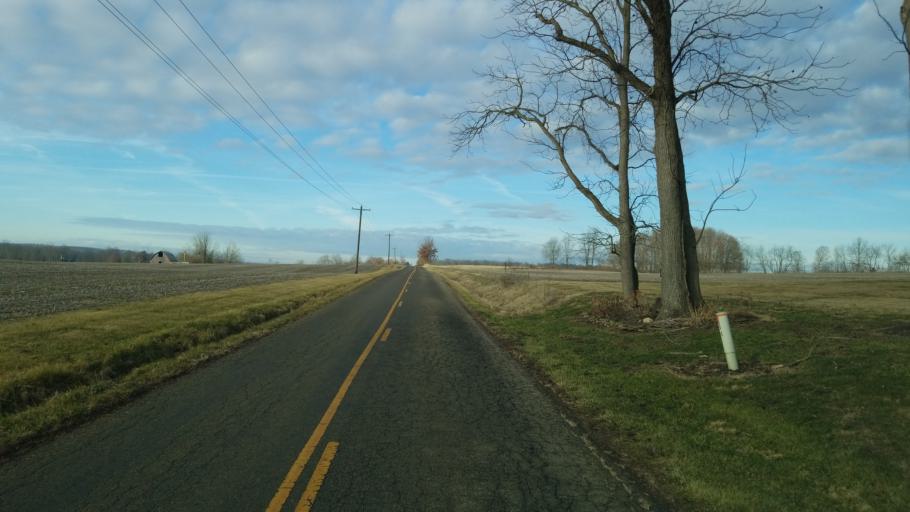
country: US
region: Ohio
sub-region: Knox County
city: Gambier
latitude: 40.3137
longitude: -82.3372
